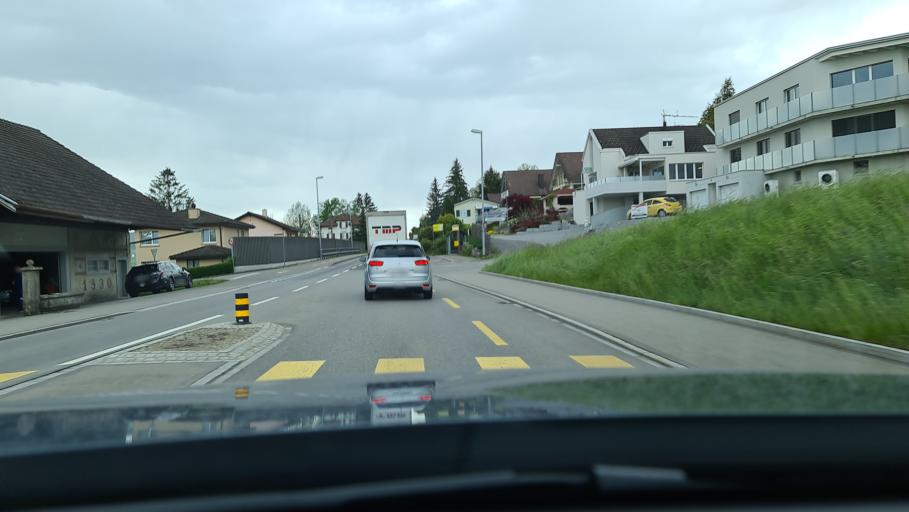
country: CH
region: Lucerne
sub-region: Sursee District
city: Geuensee
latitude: 47.2061
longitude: 8.1012
